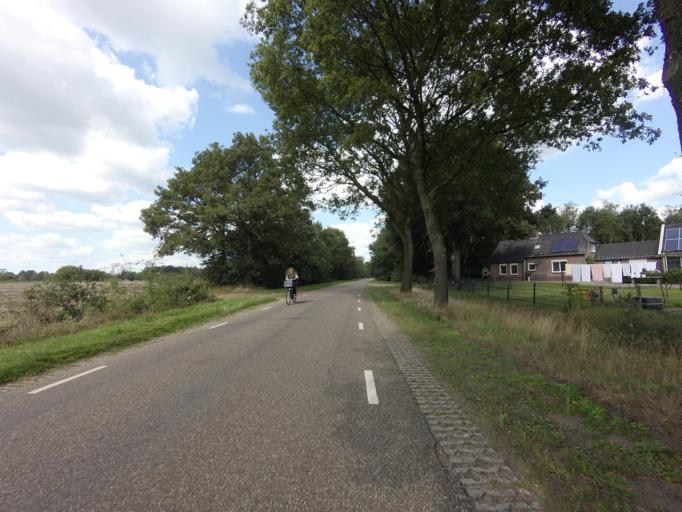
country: NL
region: Drenthe
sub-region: Gemeente Westerveld
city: Dwingeloo
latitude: 52.8652
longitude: 6.3764
